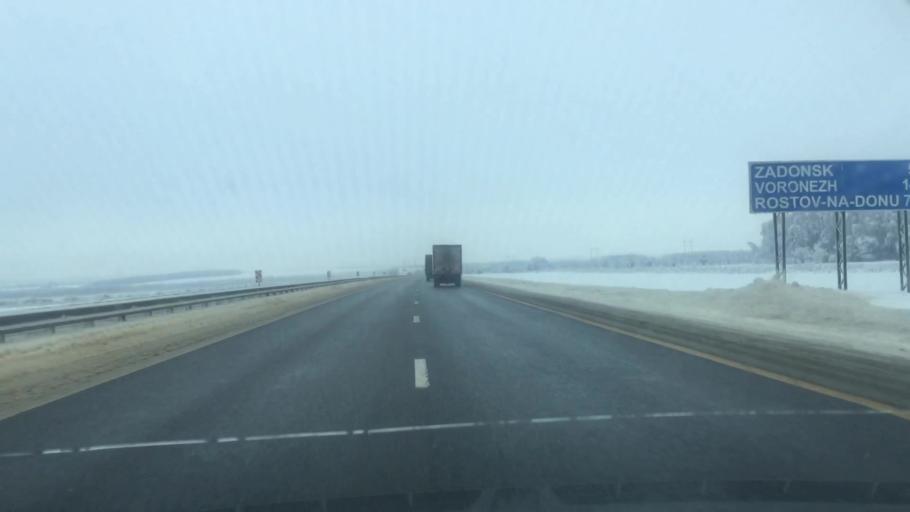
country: RU
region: Lipetsk
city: Stanovoye
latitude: 52.7419
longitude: 38.4758
